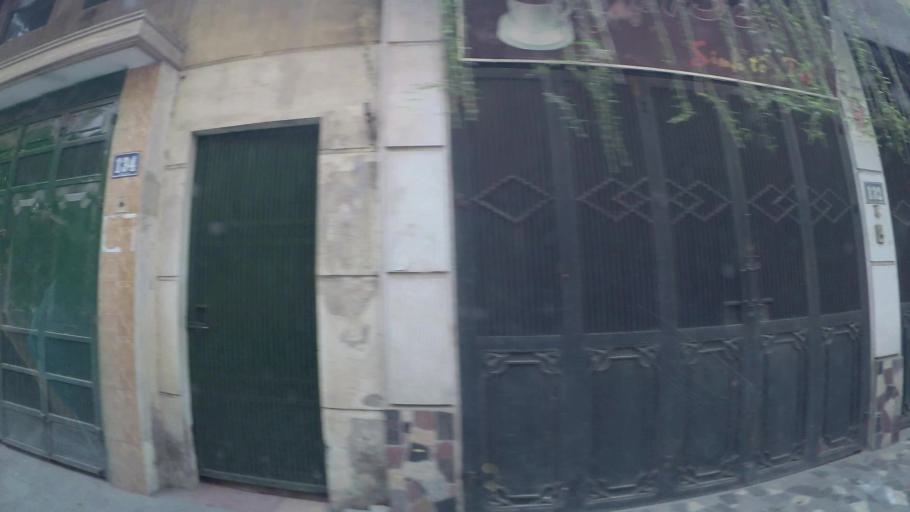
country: VN
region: Ha Noi
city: Dong Da
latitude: 20.9919
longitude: 105.8285
